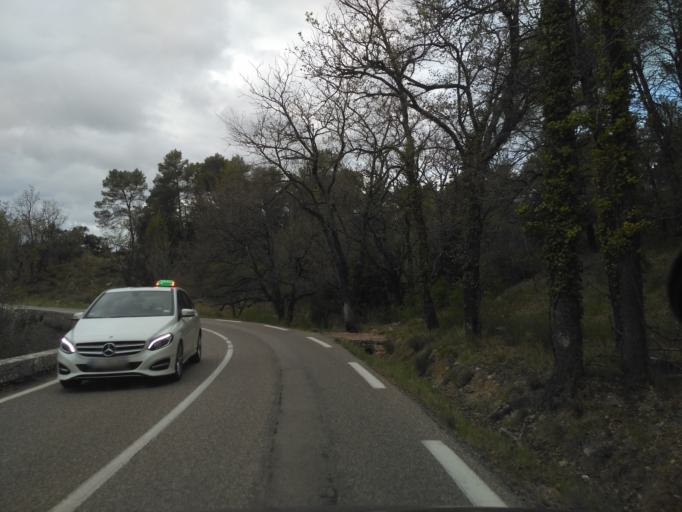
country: FR
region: Provence-Alpes-Cote d'Azur
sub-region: Departement du Var
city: Barjols
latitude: 43.6081
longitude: 5.9511
